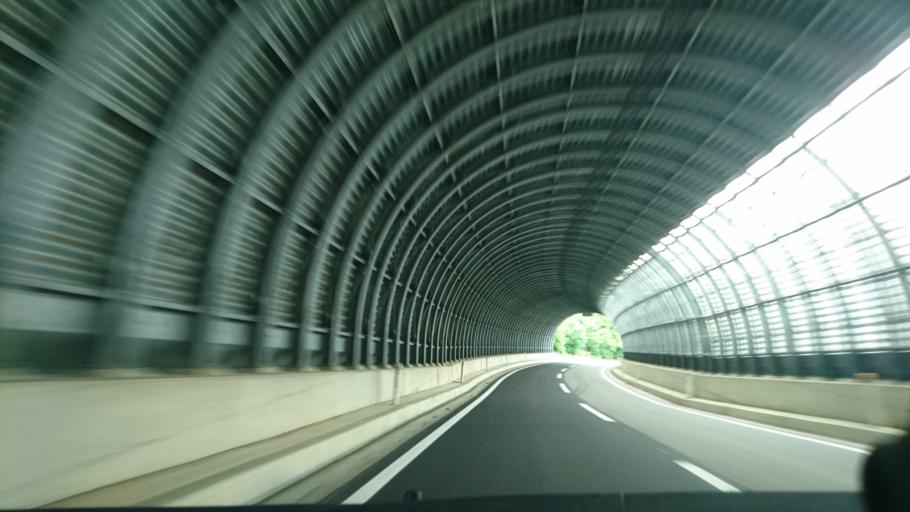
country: JP
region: Akita
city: Yuzawa
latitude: 39.1660
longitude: 140.7470
